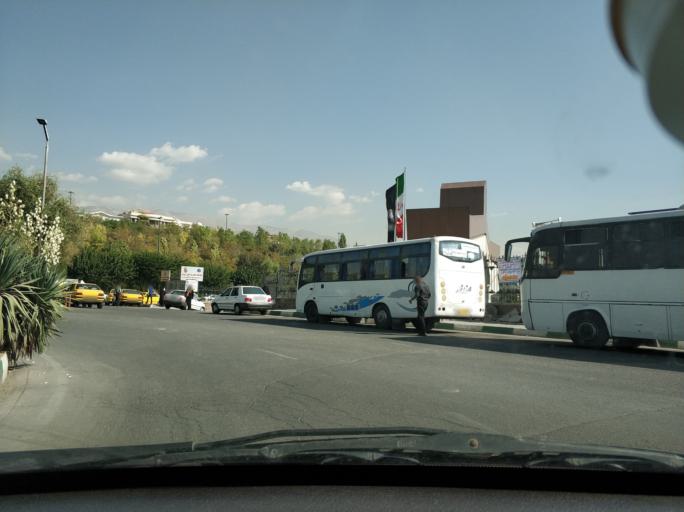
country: IR
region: Tehran
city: Tehran
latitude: 35.7489
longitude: 51.3784
